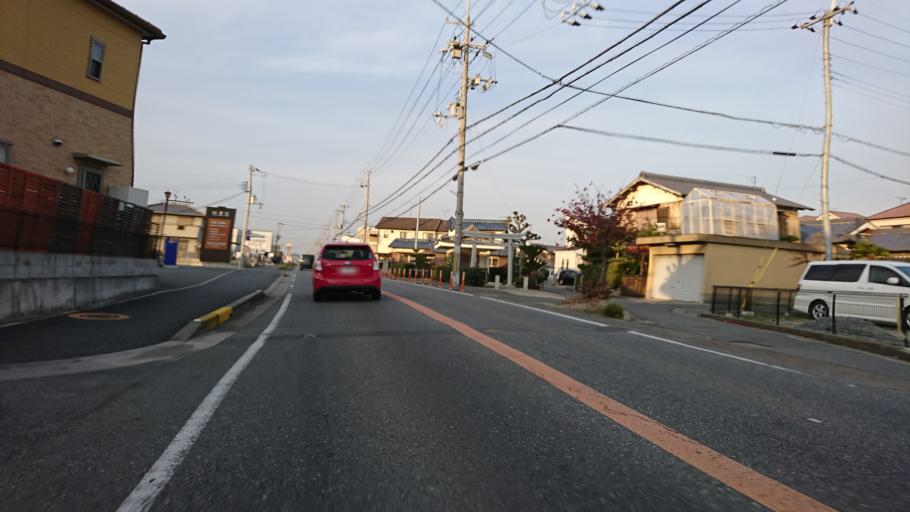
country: JP
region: Hyogo
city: Kakogawacho-honmachi
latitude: 34.7592
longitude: 134.8748
